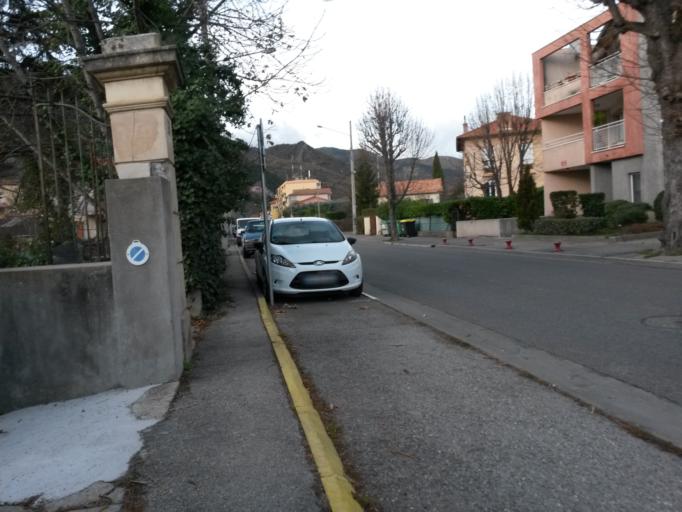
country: FR
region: Provence-Alpes-Cote d'Azur
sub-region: Departement des Alpes-de-Haute-Provence
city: Digne-les-Bains
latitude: 44.0982
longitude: 6.2330
